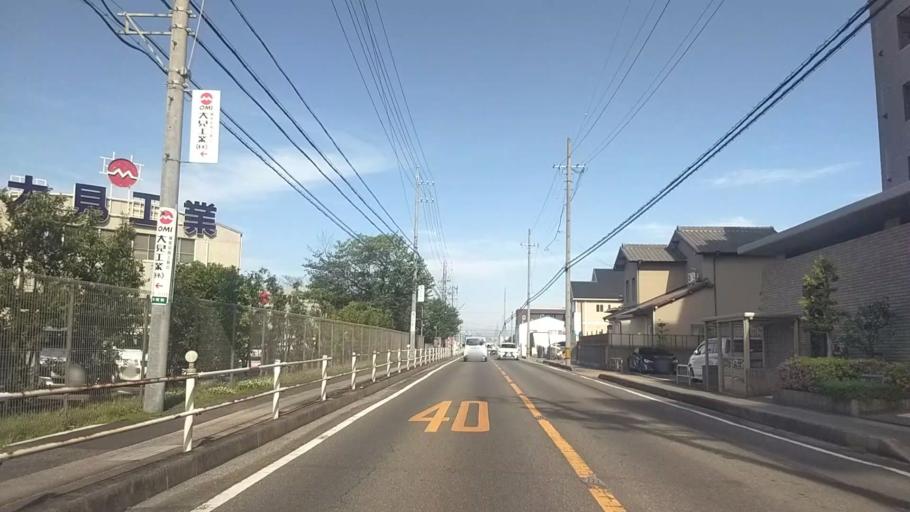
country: JP
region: Aichi
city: Anjo
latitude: 34.9585
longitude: 137.0974
